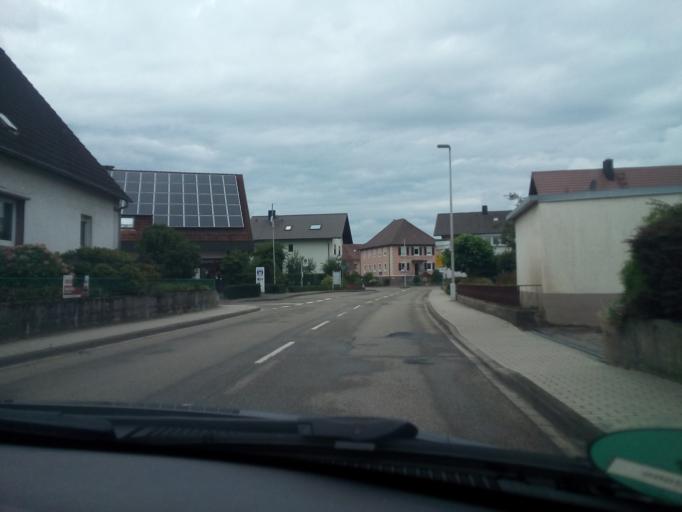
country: DE
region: Baden-Wuerttemberg
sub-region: Karlsruhe Region
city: Zell
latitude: 48.6862
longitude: 8.0587
